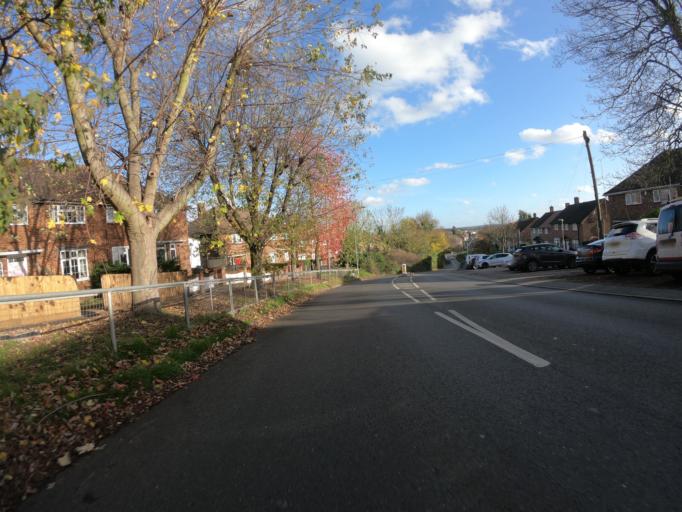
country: GB
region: England
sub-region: Greater London
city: Orpington
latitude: 51.3981
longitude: 0.0998
